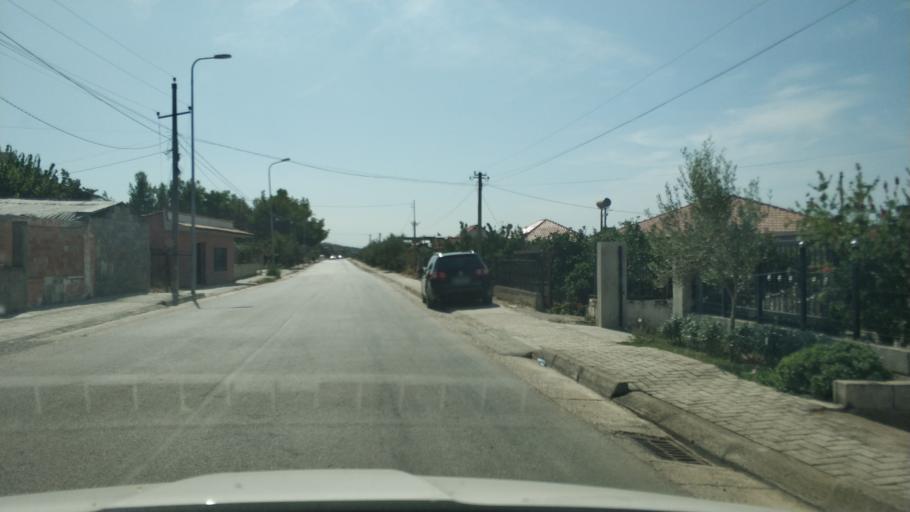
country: AL
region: Fier
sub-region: Rrethi i Lushnjes
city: Divjake
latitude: 40.9769
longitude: 19.5355
